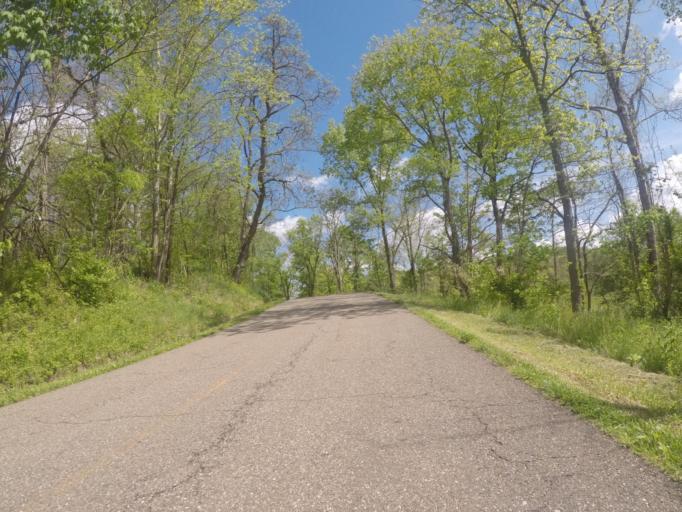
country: US
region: West Virginia
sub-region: Cabell County
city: Huntington
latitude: 38.5190
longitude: -82.4402
